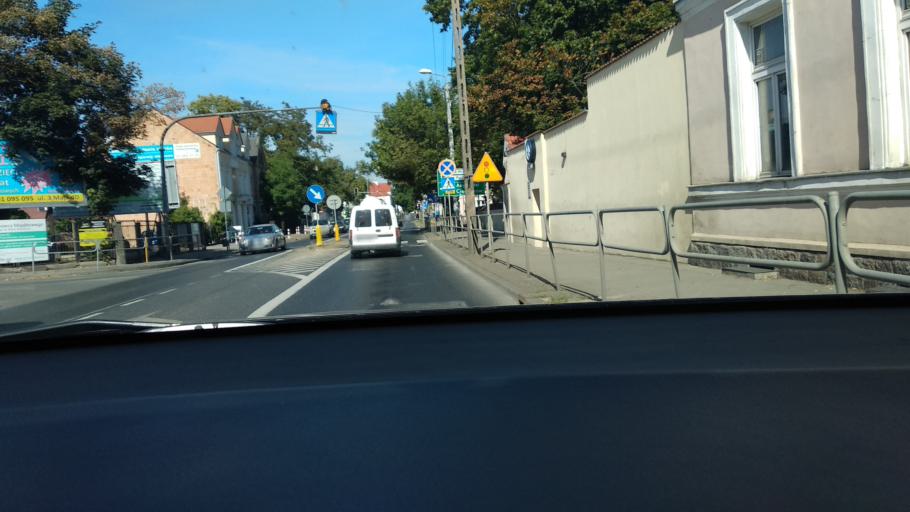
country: PL
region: Masovian Voivodeship
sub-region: Powiat pultuski
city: Pultusk
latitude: 52.7031
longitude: 21.0861
